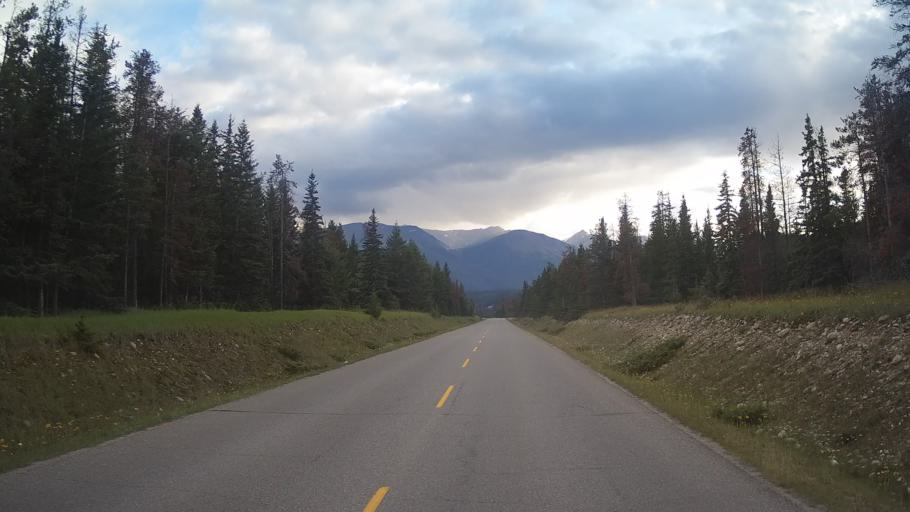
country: CA
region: Alberta
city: Jasper Park Lodge
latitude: 52.9194
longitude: -118.0421
